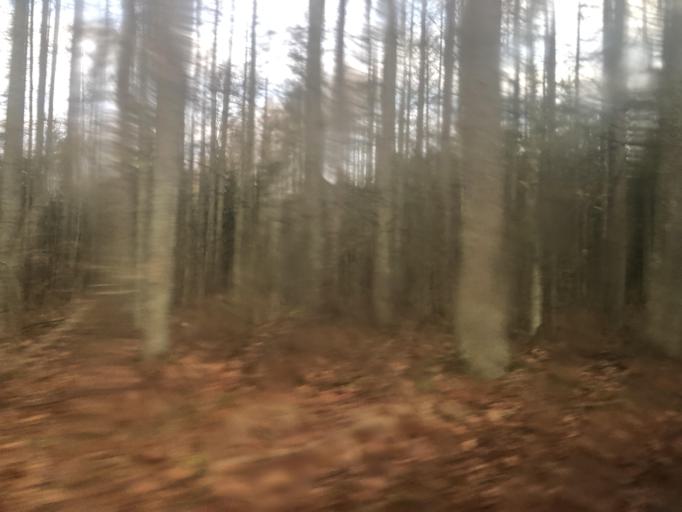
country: SE
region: Skane
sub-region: Lunds Kommun
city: Veberod
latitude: 55.6083
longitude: 13.5386
